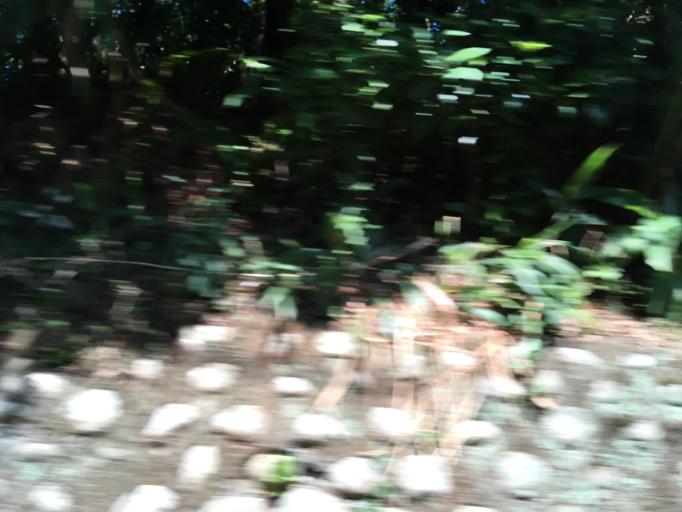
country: TW
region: Taipei
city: Taipei
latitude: 25.1527
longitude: 121.5028
